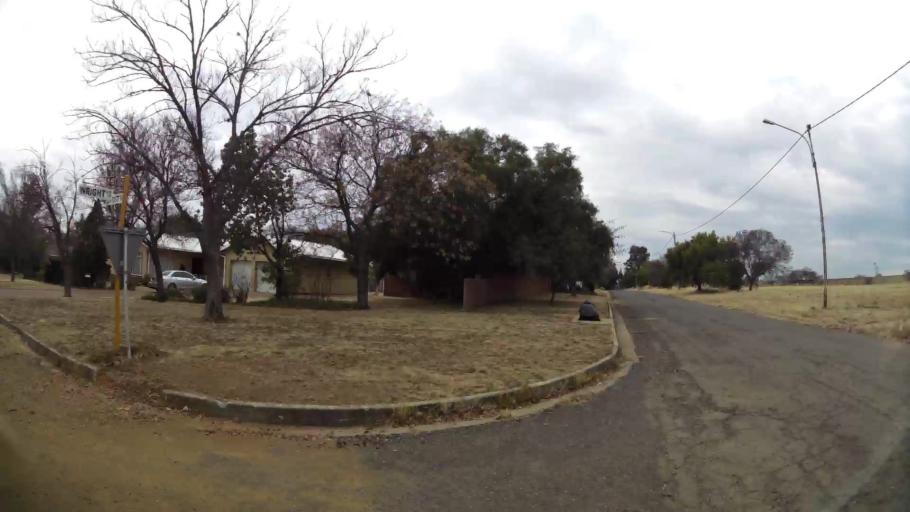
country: ZA
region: Orange Free State
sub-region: Fezile Dabi District Municipality
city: Kroonstad
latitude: -27.6818
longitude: 27.2449
